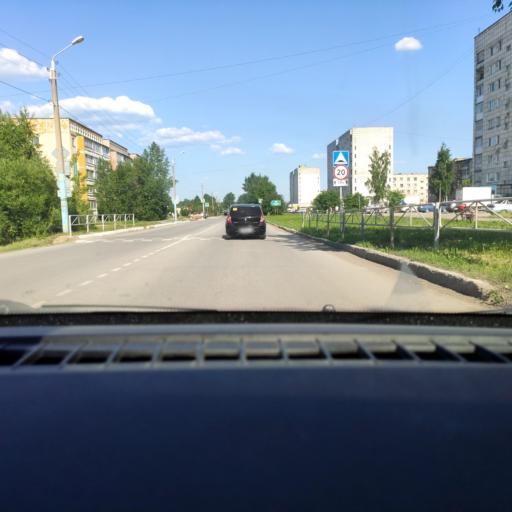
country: RU
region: Perm
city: Krasnokamsk
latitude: 58.0877
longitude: 55.7782
